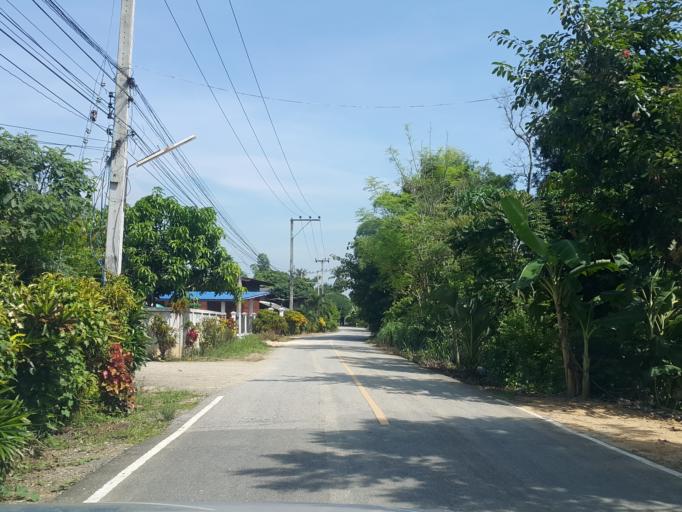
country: TH
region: Chiang Mai
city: Saraphi
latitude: 18.6867
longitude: 99.0750
